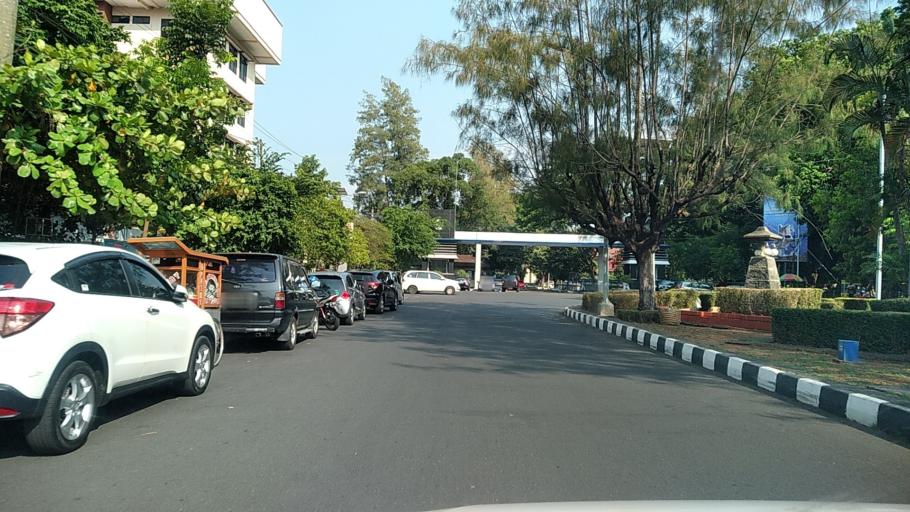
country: ID
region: Central Java
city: Semarang
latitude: -6.9941
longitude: 110.4234
